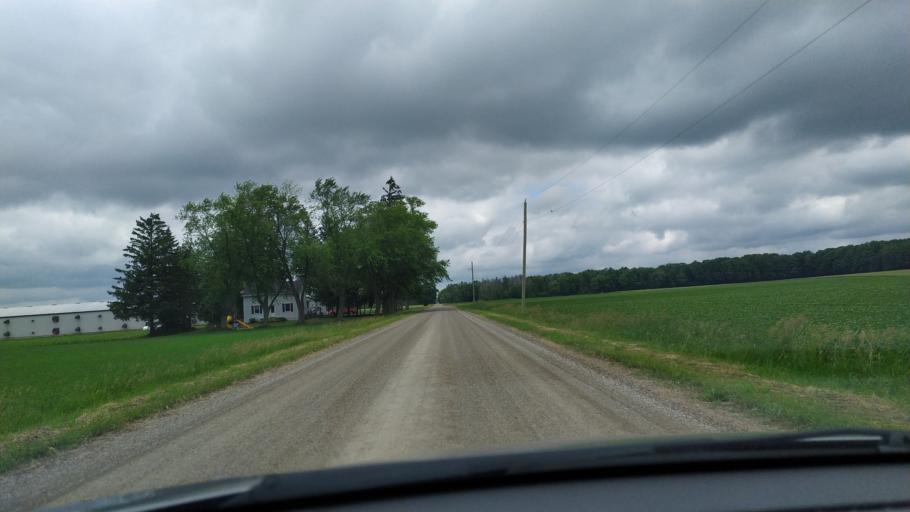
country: CA
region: Ontario
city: Stratford
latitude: 43.4093
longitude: -80.8880
